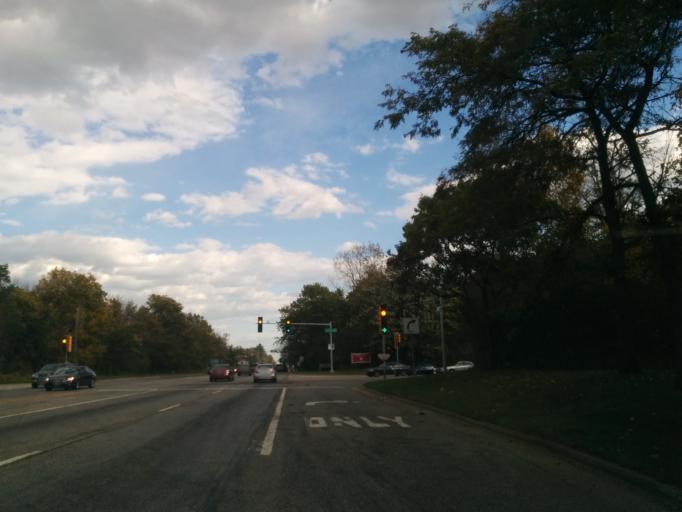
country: US
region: Illinois
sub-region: Cook County
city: Park Ridge
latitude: 42.0103
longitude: -87.8598
